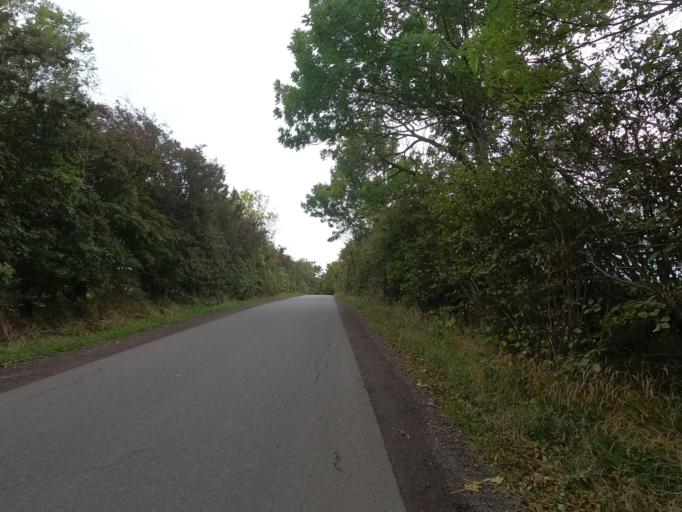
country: DE
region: Schleswig-Holstein
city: Neukirchen
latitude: 54.3523
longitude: 11.0335
